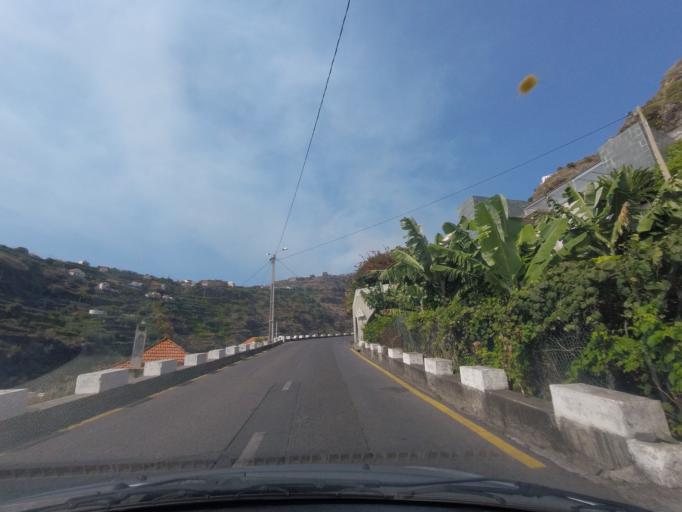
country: PT
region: Madeira
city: Ribeira Brava
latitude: 32.6717
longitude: -17.0632
